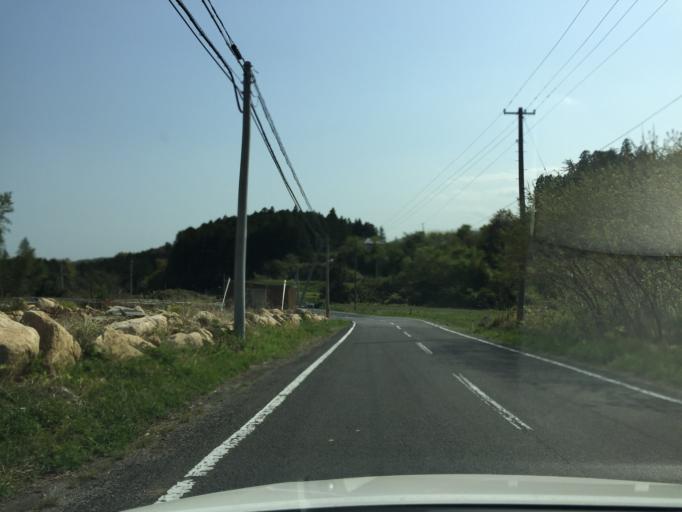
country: JP
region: Fukushima
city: Iwaki
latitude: 37.1440
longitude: 140.8540
